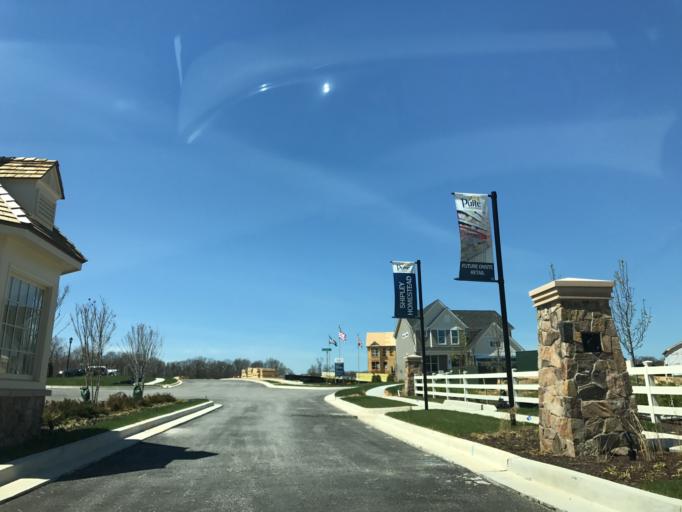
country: US
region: Maryland
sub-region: Anne Arundel County
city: Fort Meade
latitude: 39.1335
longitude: -76.7354
